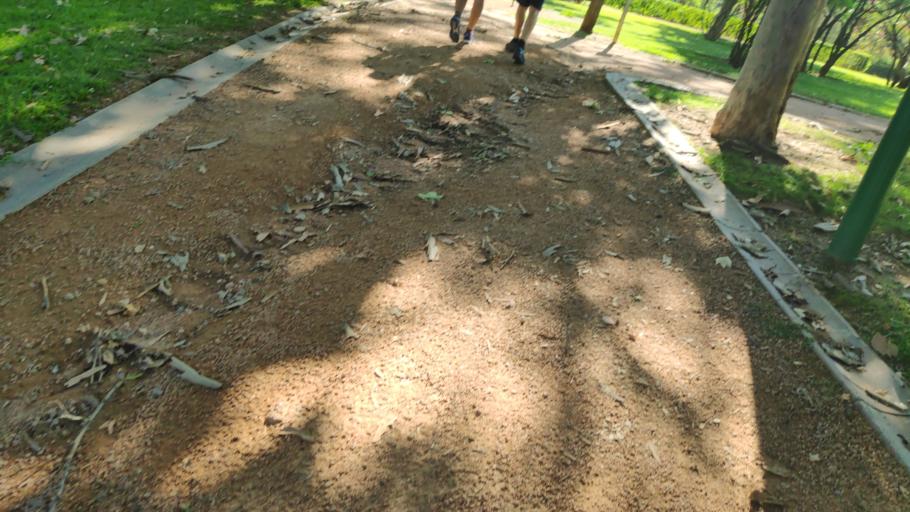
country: ES
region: Andalusia
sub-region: Province of Cordoba
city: Cordoba
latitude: 37.8726
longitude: -4.7881
